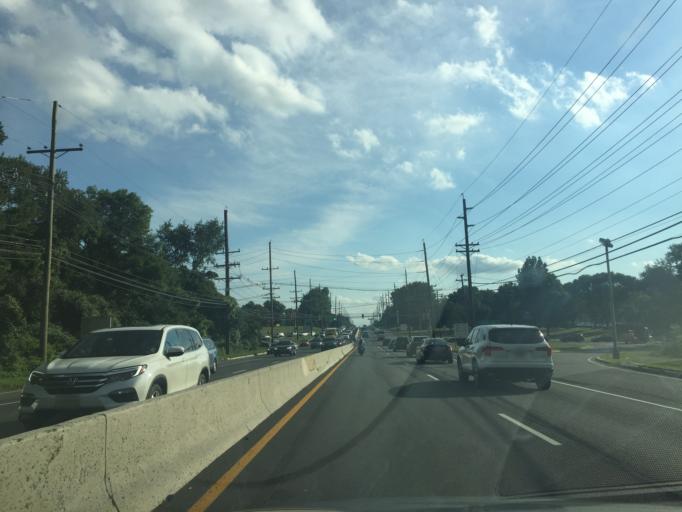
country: US
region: New Jersey
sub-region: Somerset County
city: Kingston
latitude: 40.3674
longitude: -74.5946
